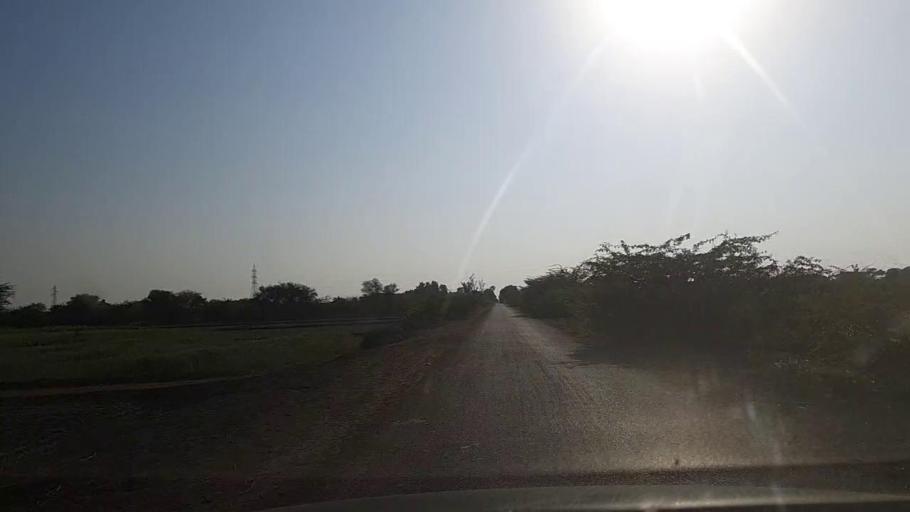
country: PK
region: Sindh
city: Naukot
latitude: 24.9997
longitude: 69.2672
